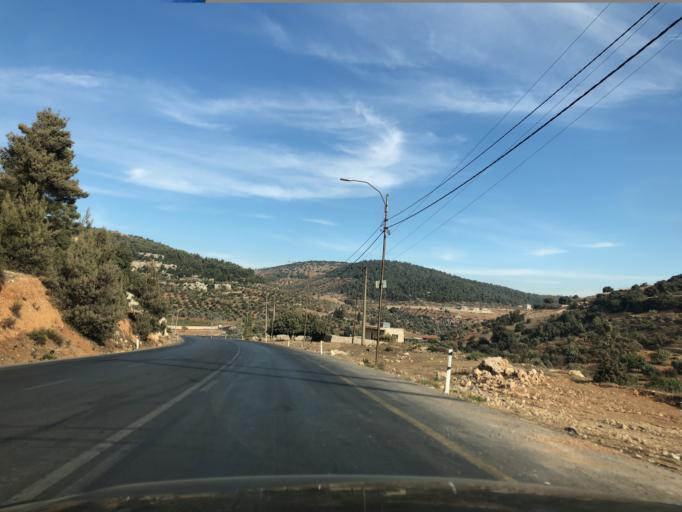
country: JO
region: Irbid
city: `Anjarah
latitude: 32.2986
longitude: 35.7813
